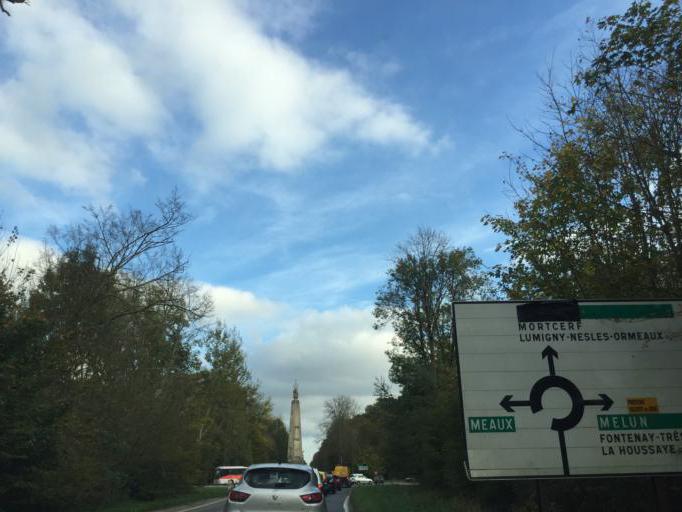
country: FR
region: Ile-de-France
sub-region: Departement de Seine-et-Marne
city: La Houssaye-en-Brie
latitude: 48.7923
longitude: 2.8679
